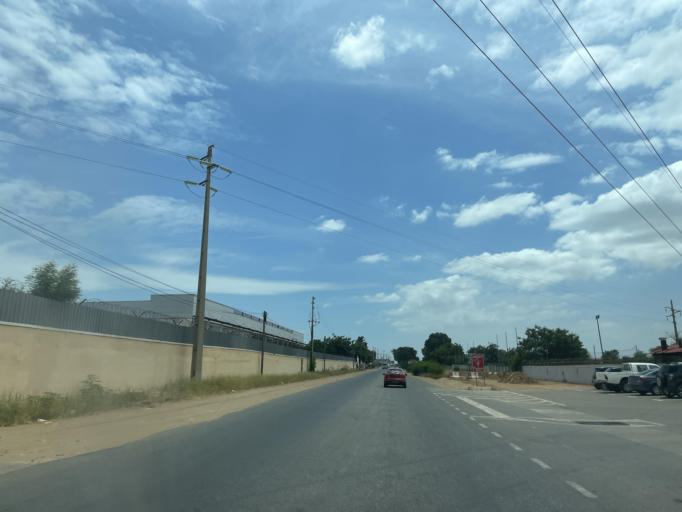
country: AO
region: Luanda
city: Luanda
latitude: -8.9332
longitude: 13.3924
